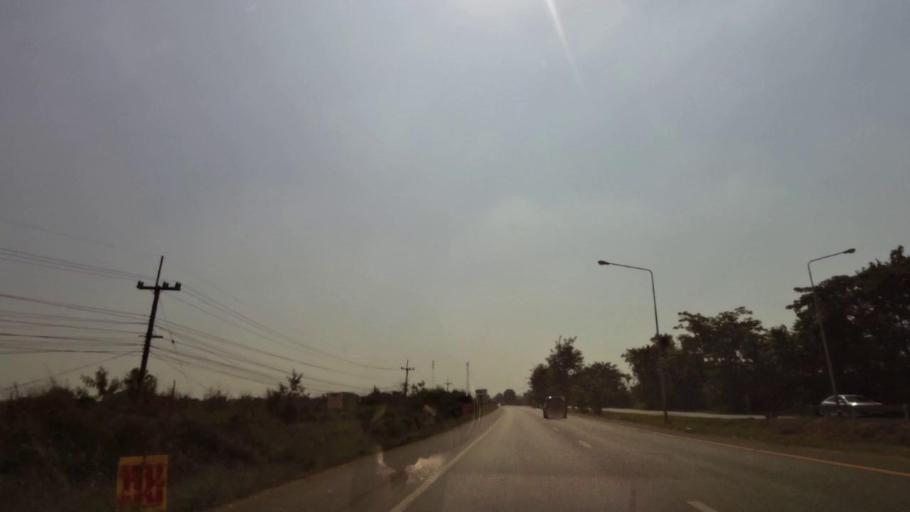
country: TH
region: Phichit
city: Wachira Barami
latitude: 16.3521
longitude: 100.1286
